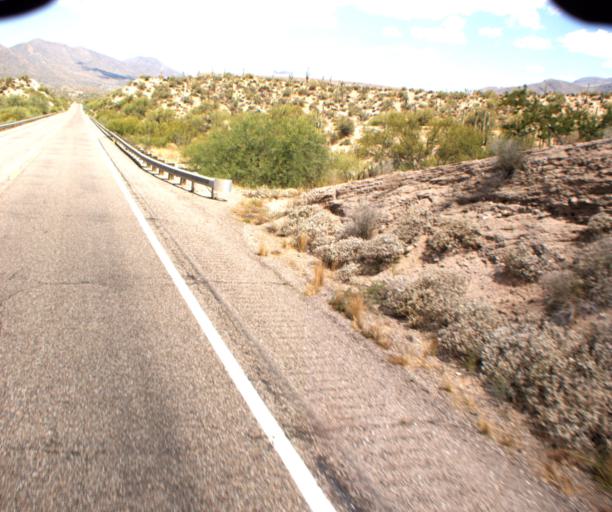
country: US
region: Arizona
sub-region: Pinal County
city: Kearny
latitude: 33.1024
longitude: -110.9395
